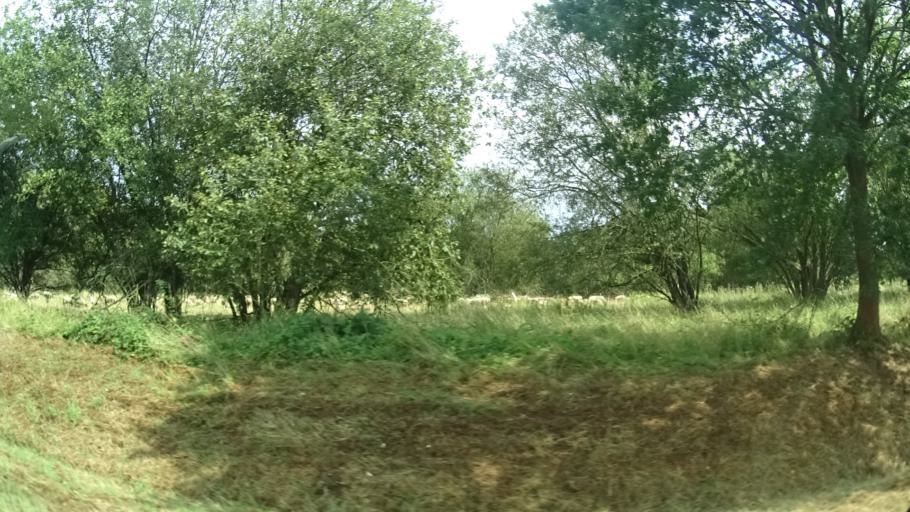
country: DE
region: Hesse
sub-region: Regierungsbezirk Kassel
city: Niederaula
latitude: 50.7729
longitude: 9.5985
